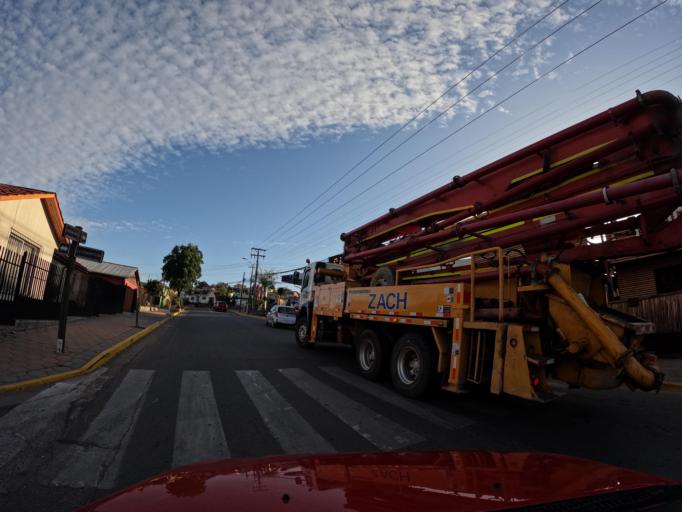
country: CL
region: Valparaiso
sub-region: San Antonio Province
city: San Antonio
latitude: -34.1170
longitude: -71.7295
